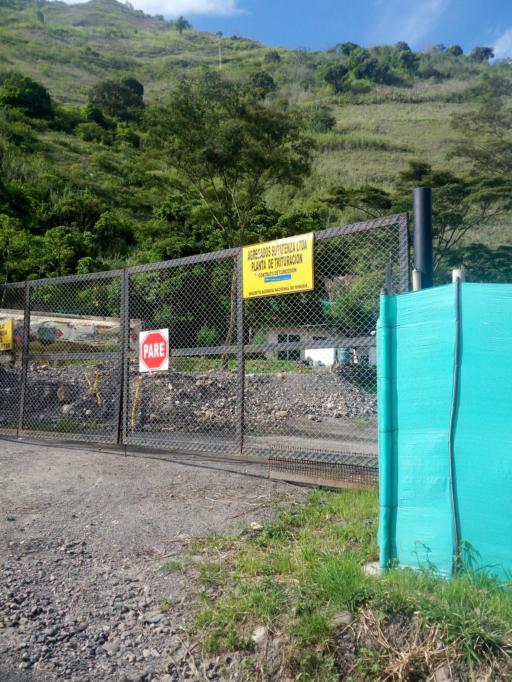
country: CO
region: Boyaca
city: Somondoco
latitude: 5.0114
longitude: -73.4322
